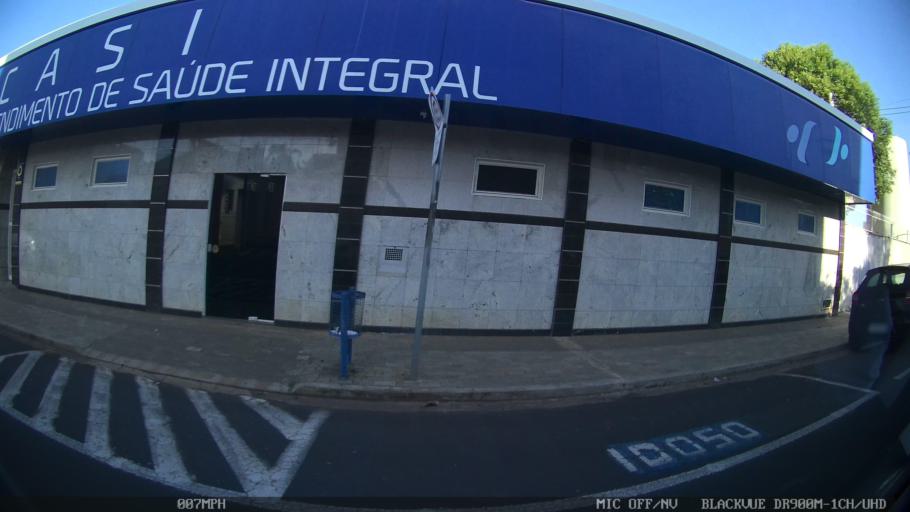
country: BR
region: Sao Paulo
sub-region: Sao Jose Do Rio Preto
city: Sao Jose do Rio Preto
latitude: -20.8135
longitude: -49.3924
